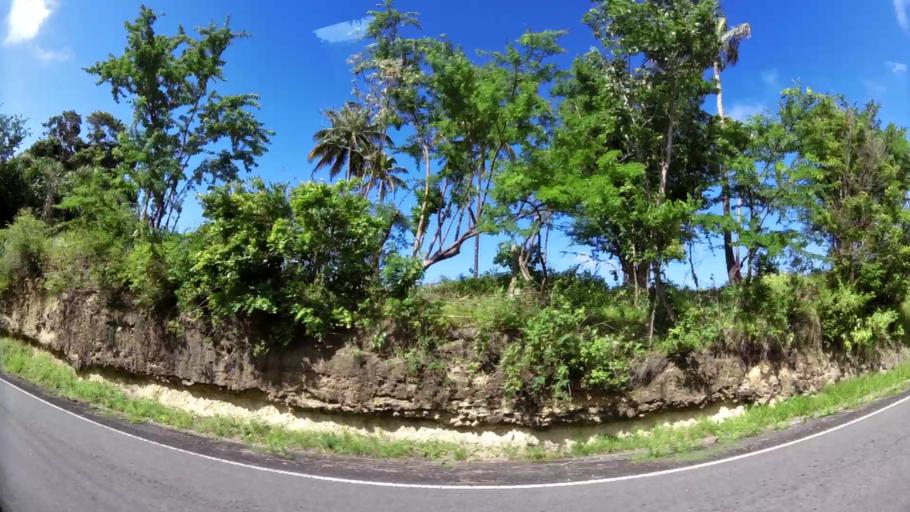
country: LC
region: Choiseul Quarter
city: Choiseul
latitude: 13.7902
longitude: -61.0397
